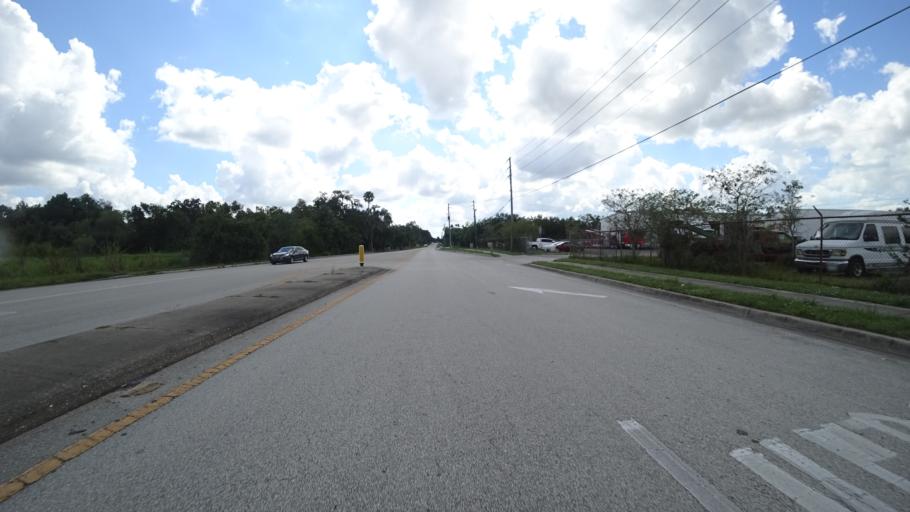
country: US
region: Florida
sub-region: Manatee County
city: Samoset
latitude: 27.4464
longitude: -82.5220
